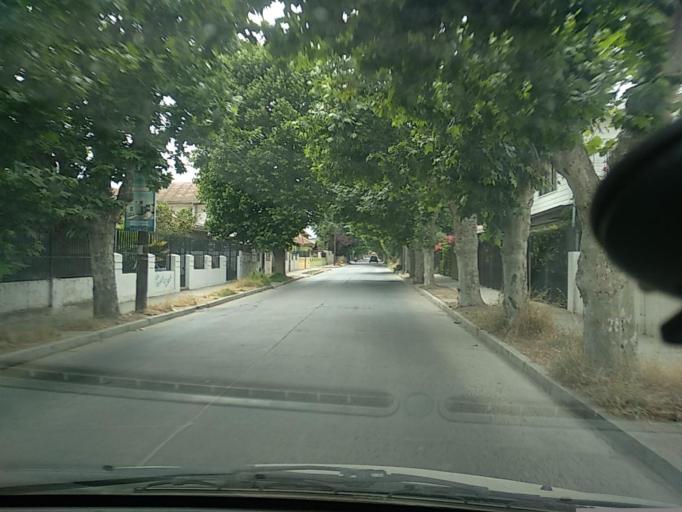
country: CL
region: Valparaiso
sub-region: Provincia de Marga Marga
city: Villa Alemana
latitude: -33.0400
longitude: -71.3731
